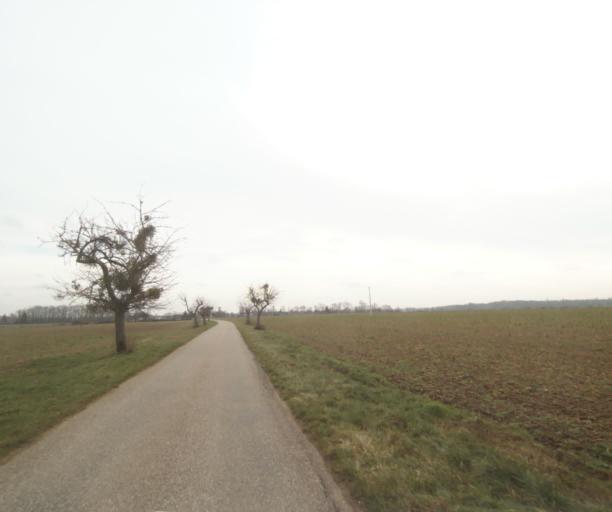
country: FR
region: Champagne-Ardenne
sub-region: Departement de la Haute-Marne
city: Villiers-en-Lieu
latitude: 48.6720
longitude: 4.8839
